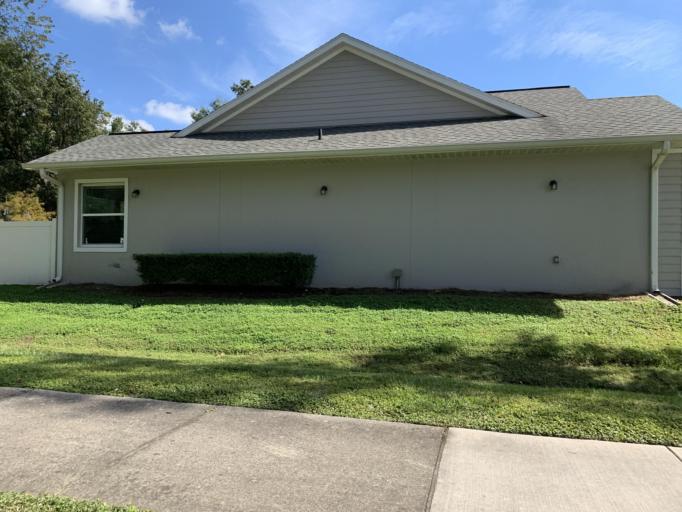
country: US
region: Florida
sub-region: Marion County
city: Ocala
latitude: 29.1789
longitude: -82.1342
